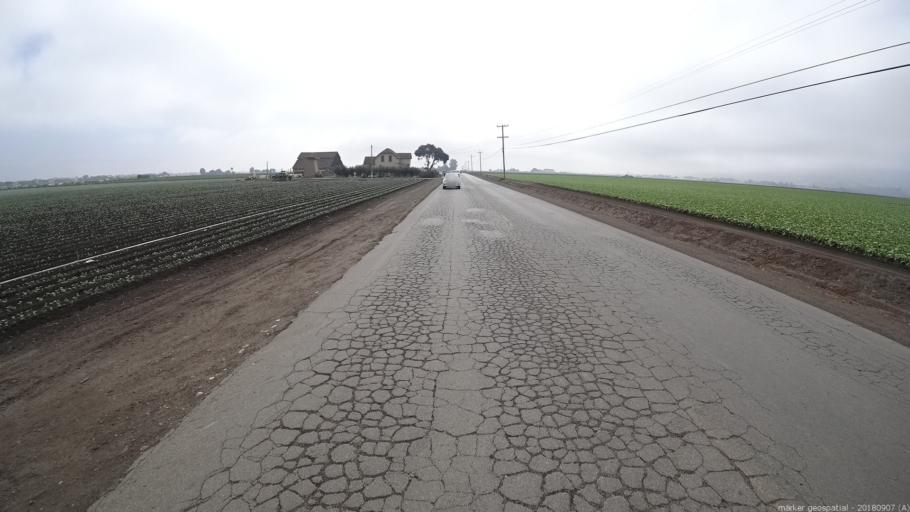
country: US
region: California
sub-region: Monterey County
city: Salinas
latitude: 36.6497
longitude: -121.6741
